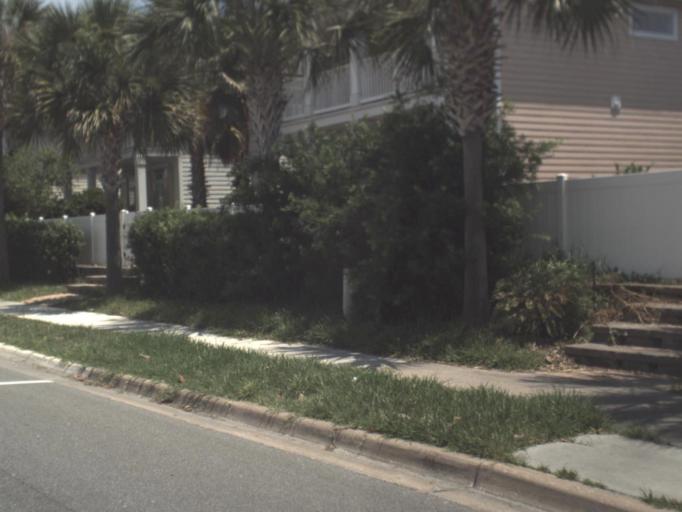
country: US
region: Florida
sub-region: Duval County
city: Neptune Beach
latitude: 30.3123
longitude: -81.3964
